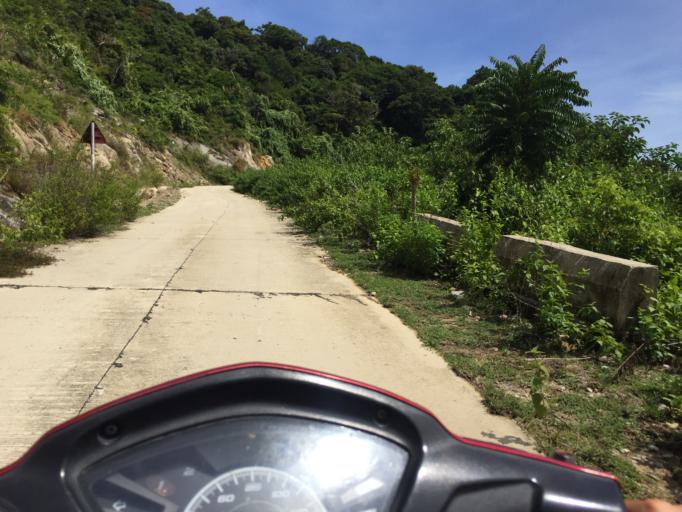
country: VN
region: Quang Nam
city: Hoi An
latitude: 15.9716
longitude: 108.5062
